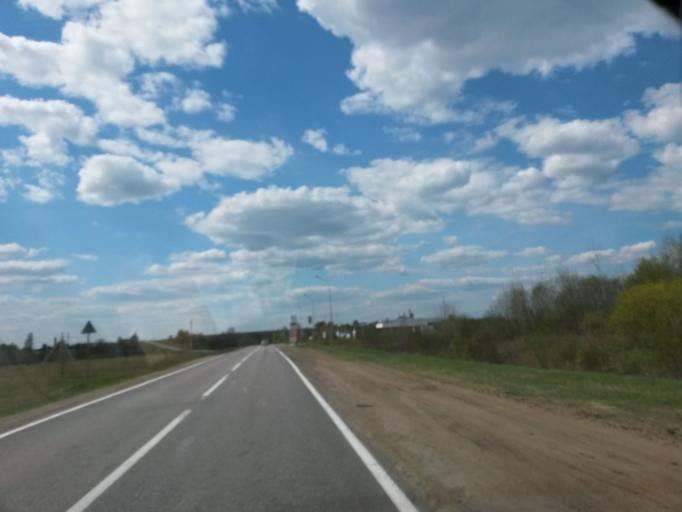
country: RU
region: Jaroslavl
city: Bol'shoye Selo
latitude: 57.7252
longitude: 38.9936
